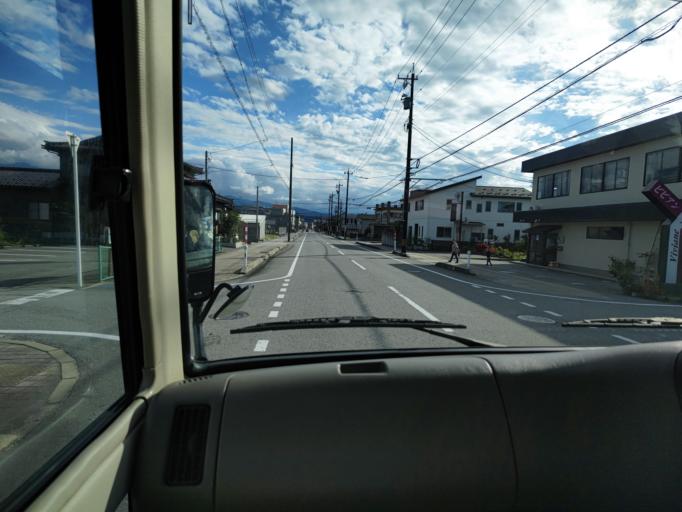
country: JP
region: Toyama
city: Nyuzen
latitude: 36.8755
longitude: 137.4468
